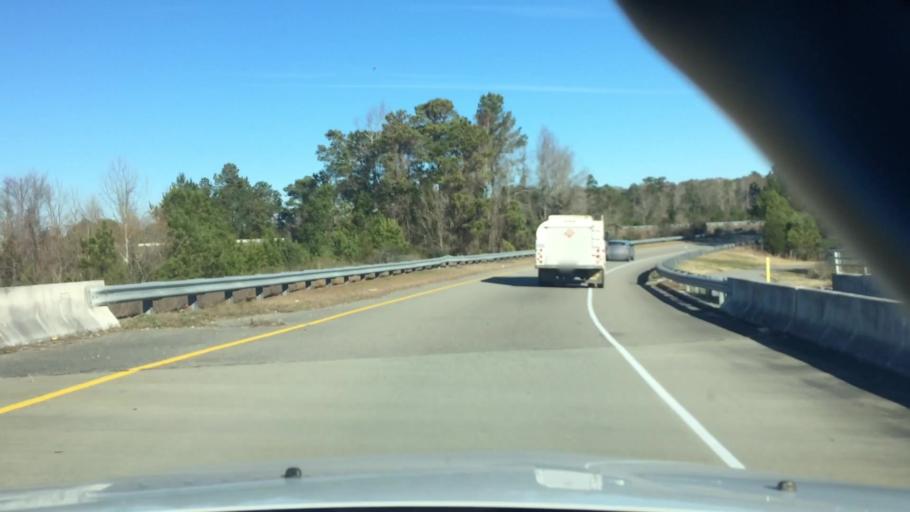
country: US
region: South Carolina
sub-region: Horry County
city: Myrtle Beach
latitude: 33.7527
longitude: -78.8510
